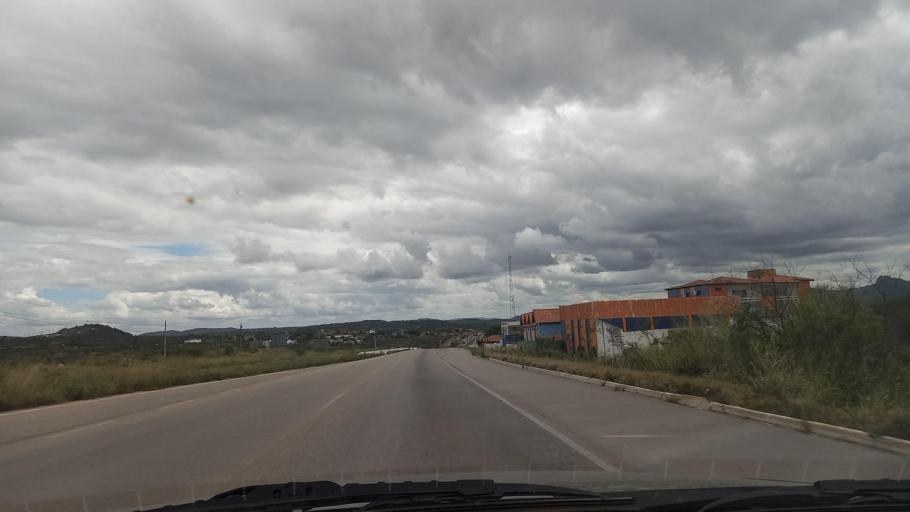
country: BR
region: Pernambuco
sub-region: Caruaru
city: Caruaru
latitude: -8.3172
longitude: -36.0552
